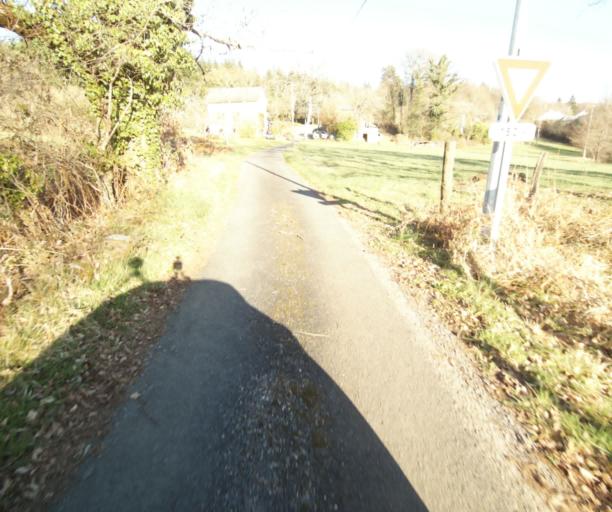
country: FR
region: Limousin
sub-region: Departement de la Correze
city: Seilhac
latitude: 45.3563
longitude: 1.7040
